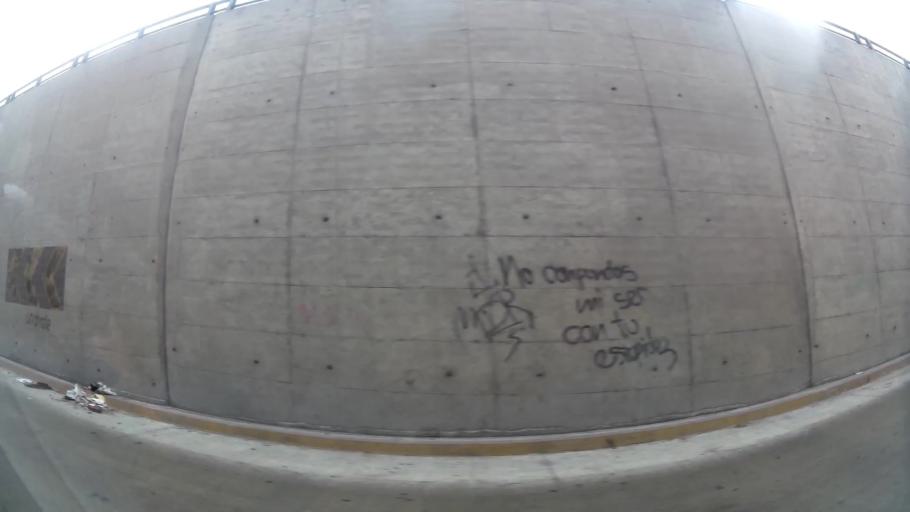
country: PE
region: Lima
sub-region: Lima
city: Santa Maria
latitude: -12.0178
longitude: -76.8951
